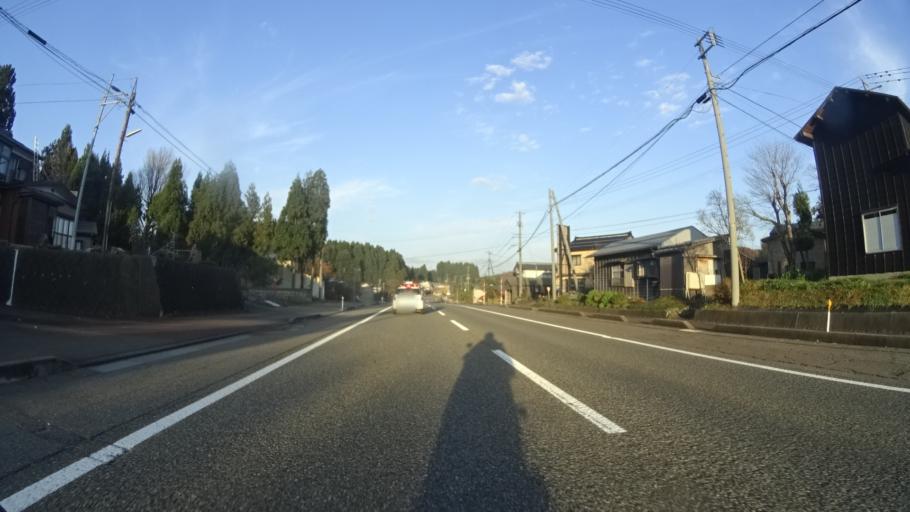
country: JP
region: Niigata
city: Nagaoka
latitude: 37.4351
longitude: 138.7297
